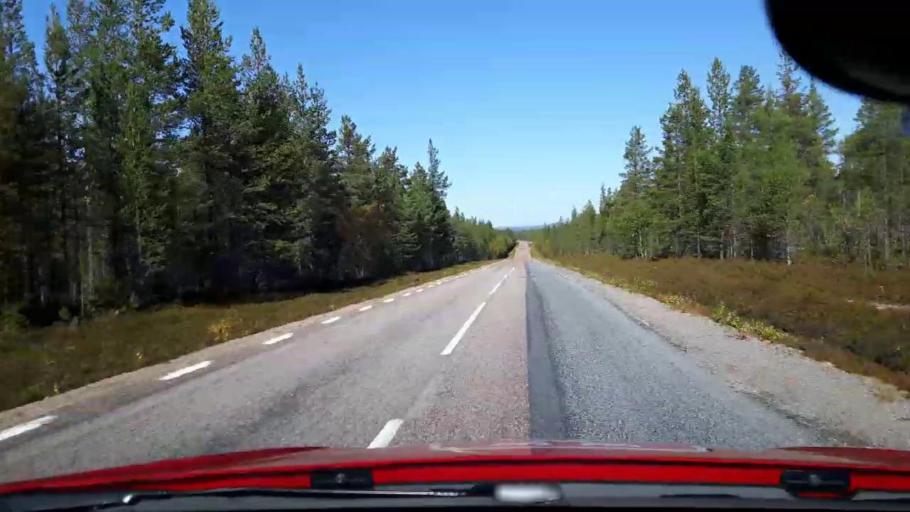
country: SE
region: Jaemtland
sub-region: Harjedalens Kommun
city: Sveg
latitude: 61.7323
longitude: 14.1645
